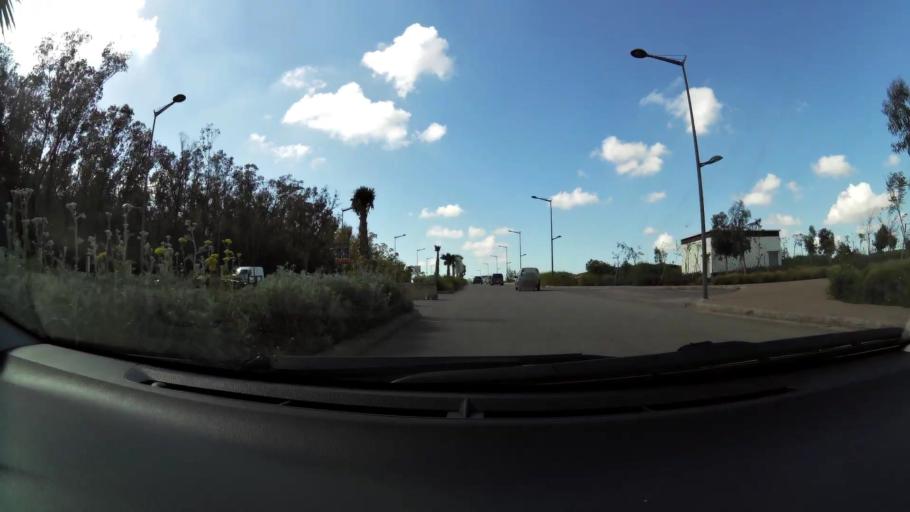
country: MA
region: Grand Casablanca
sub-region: Nouaceur
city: Bouskoura
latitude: 33.4794
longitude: -7.6226
